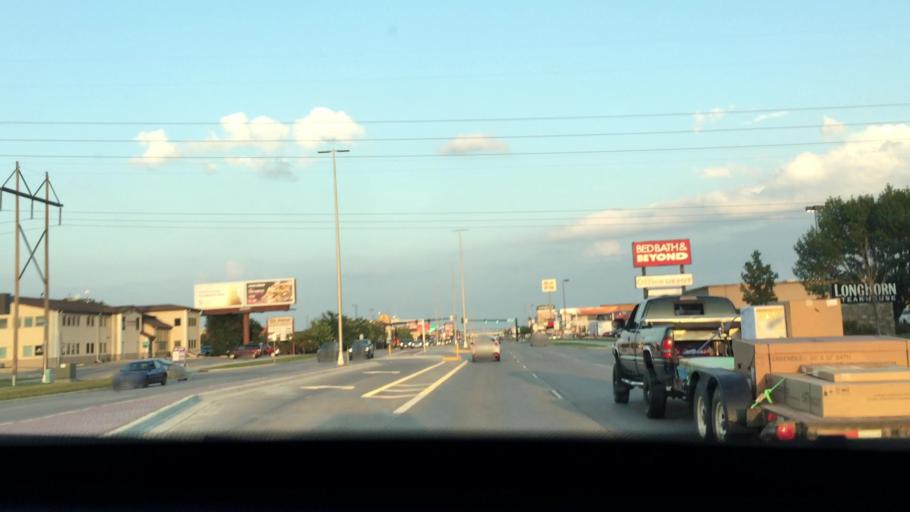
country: US
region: North Dakota
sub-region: Cass County
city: West Fargo
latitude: 46.8618
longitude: -96.8603
